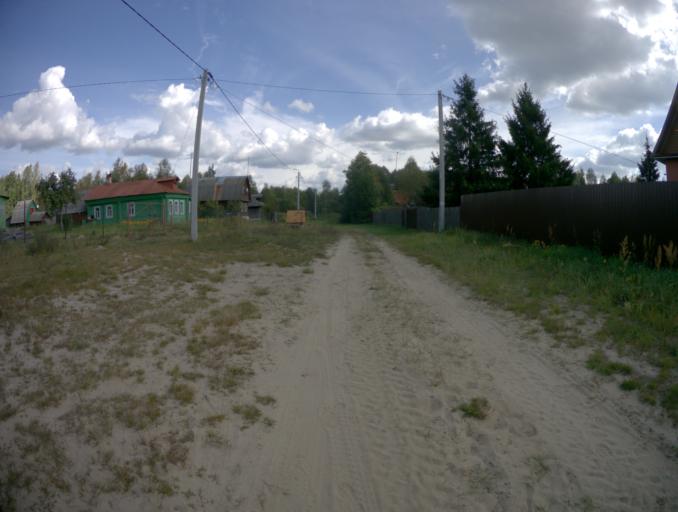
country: RU
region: Vladimir
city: Petushki
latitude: 55.8560
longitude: 39.3414
